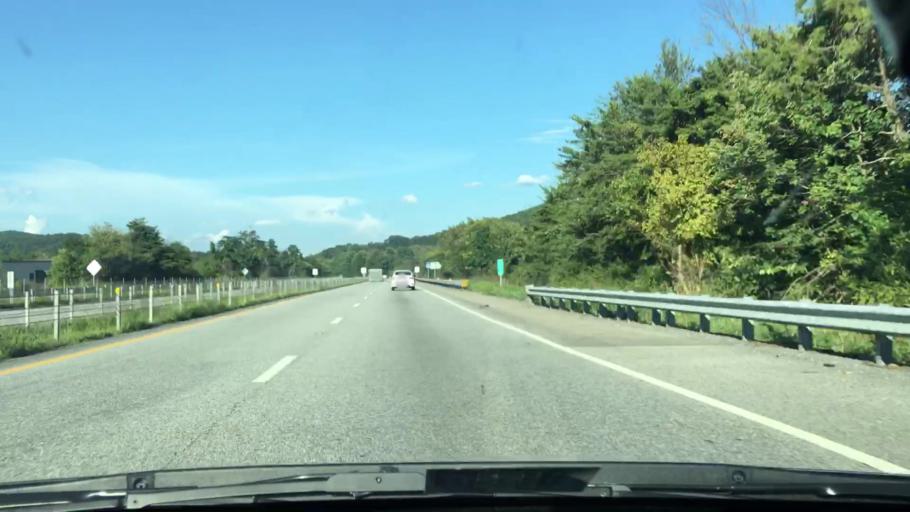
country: US
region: Virginia
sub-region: Alleghany County
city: Clifton Forge
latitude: 37.7944
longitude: -79.8785
